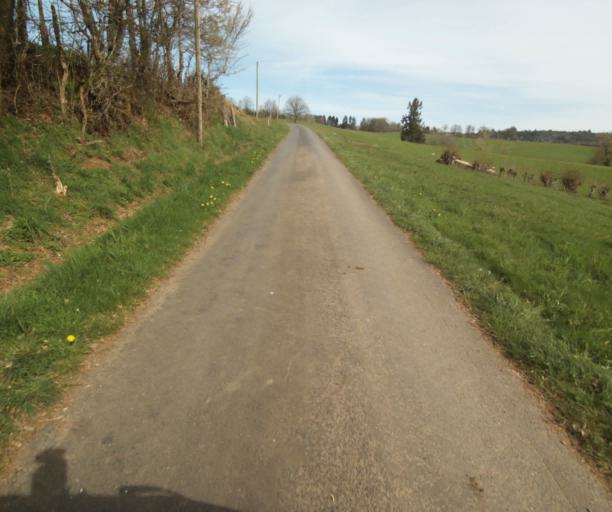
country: FR
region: Limousin
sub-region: Departement de la Correze
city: Correze
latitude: 45.3749
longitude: 1.8214
